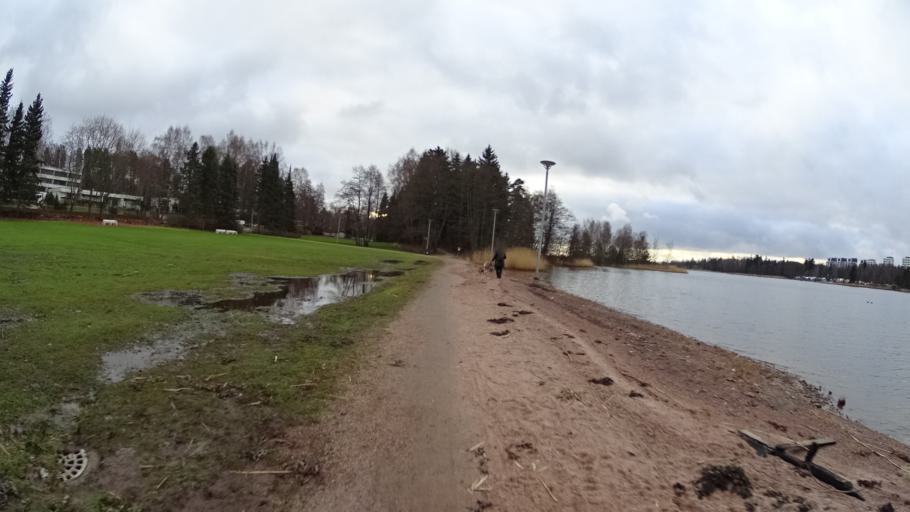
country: FI
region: Uusimaa
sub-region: Helsinki
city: Otaniemi
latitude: 60.1759
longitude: 24.8226
